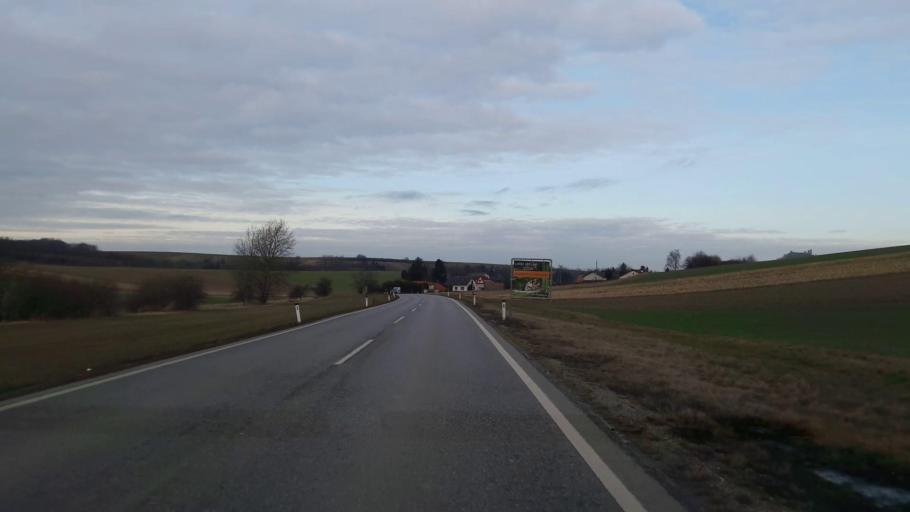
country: AT
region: Lower Austria
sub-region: Politischer Bezirk Mistelbach
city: Staatz
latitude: 48.6561
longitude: 16.4991
